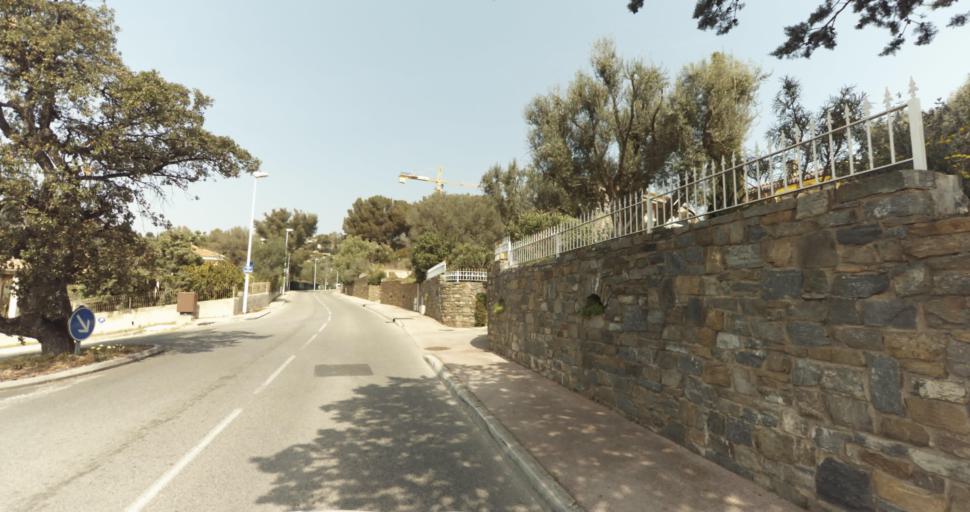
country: FR
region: Provence-Alpes-Cote d'Azur
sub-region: Departement du Var
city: Bormes-les-Mimosas
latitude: 43.1412
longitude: 6.3522
